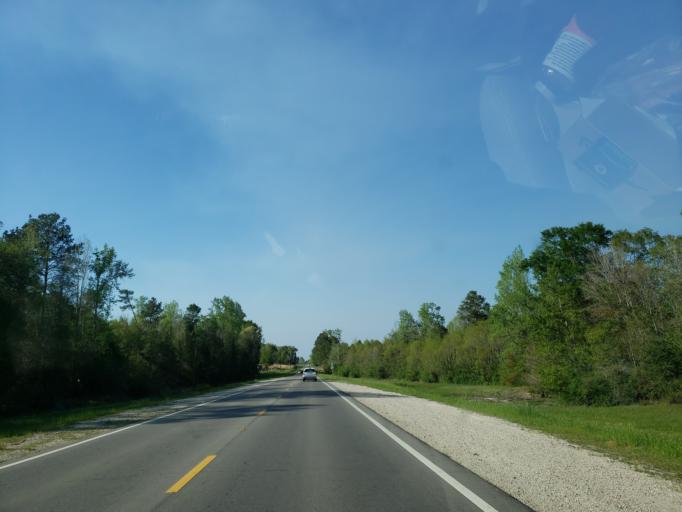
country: US
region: Mississippi
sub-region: Perry County
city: Richton
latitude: 31.3617
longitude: -88.9355
